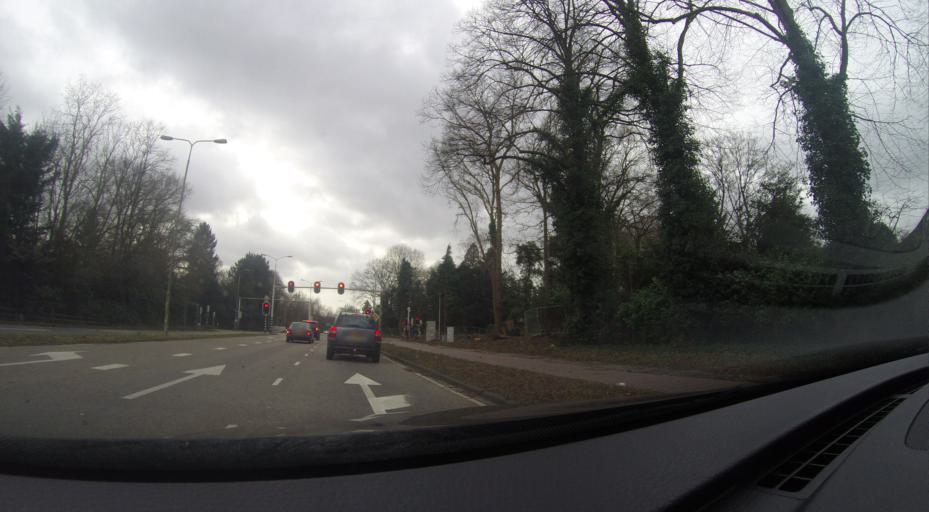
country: NL
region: North Holland
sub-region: Gemeente Laren
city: Laren
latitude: 52.2488
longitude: 5.2109
